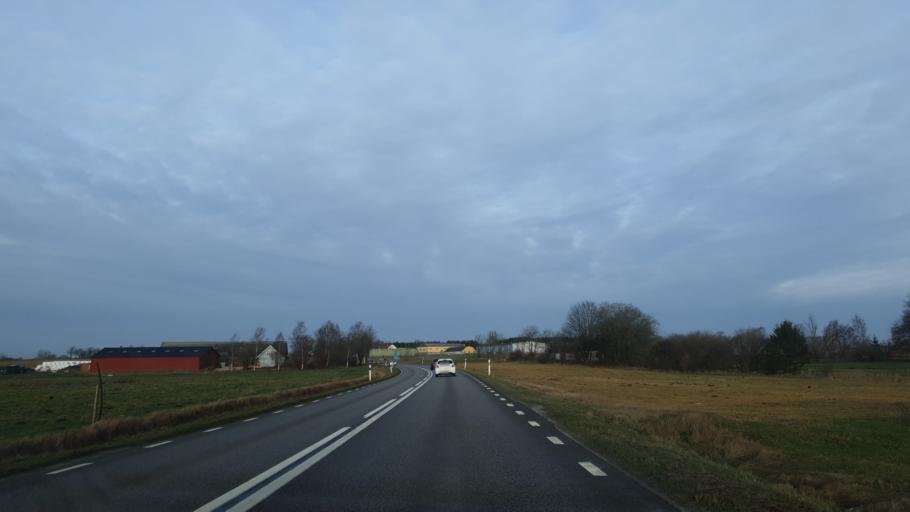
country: SE
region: Skane
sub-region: Horby Kommun
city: Hoerby
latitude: 55.7864
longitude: 13.6772
